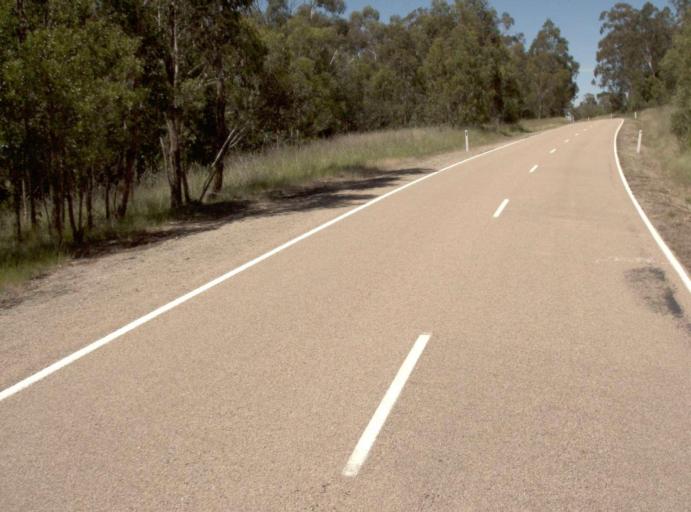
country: AU
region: Victoria
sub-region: East Gippsland
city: Lakes Entrance
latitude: -37.2113
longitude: 148.2694
